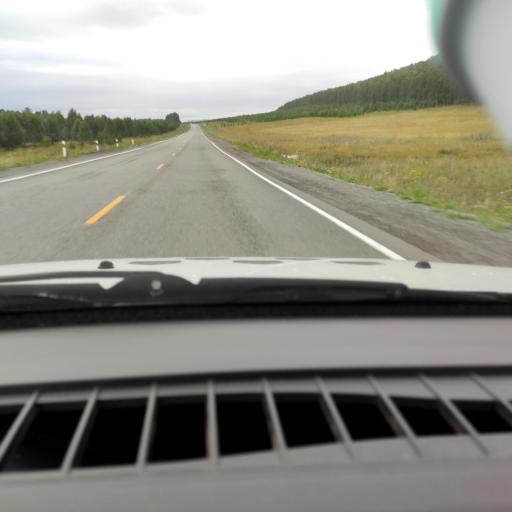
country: RU
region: Chelyabinsk
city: Karabash
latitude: 55.3461
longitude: 60.2447
